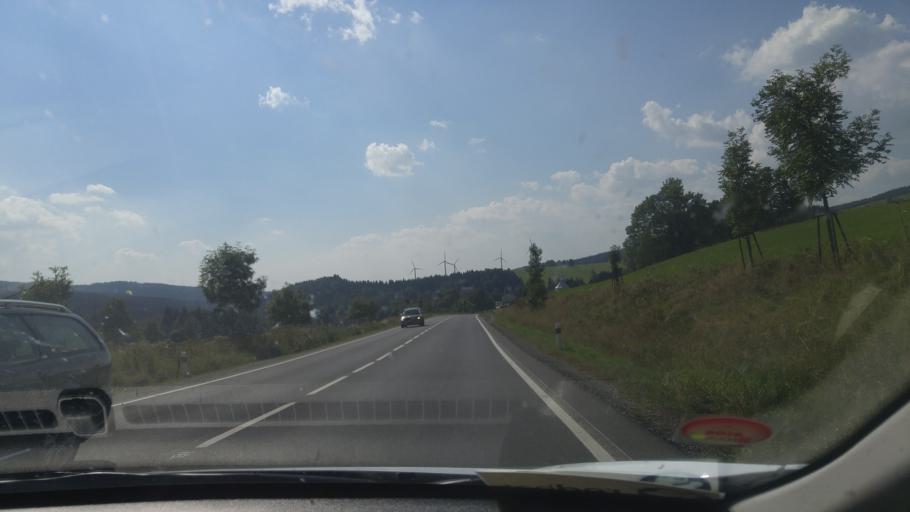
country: CZ
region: Olomoucky
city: Vapenna
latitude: 50.1897
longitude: 17.0611
